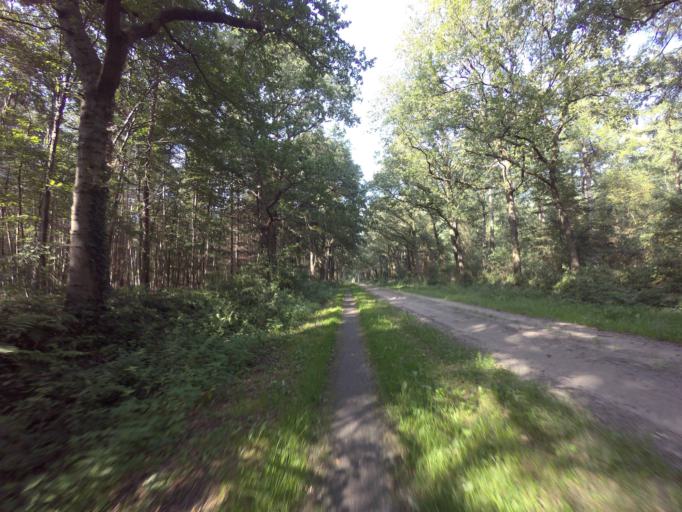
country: NL
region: Drenthe
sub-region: Gemeente Tynaarlo
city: Vries
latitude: 53.0648
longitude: 6.5069
